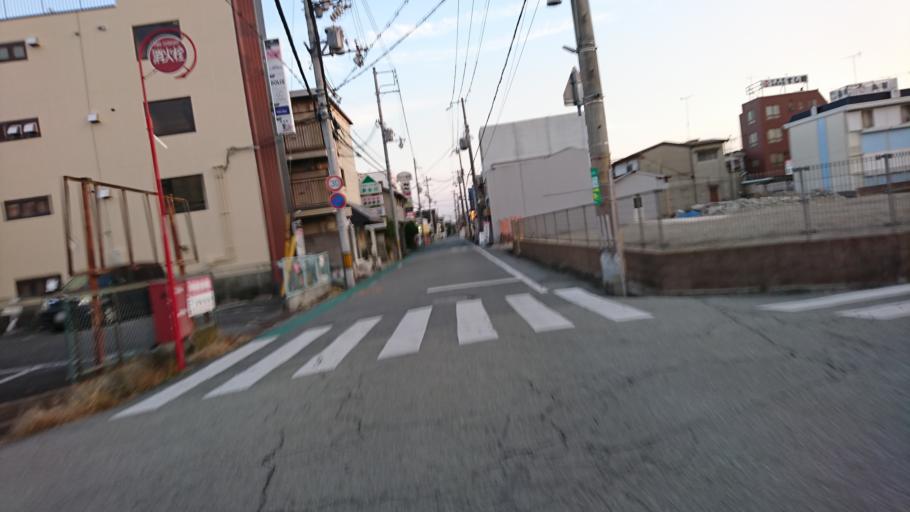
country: JP
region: Hyogo
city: Kakogawacho-honmachi
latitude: 34.7433
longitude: 134.8702
